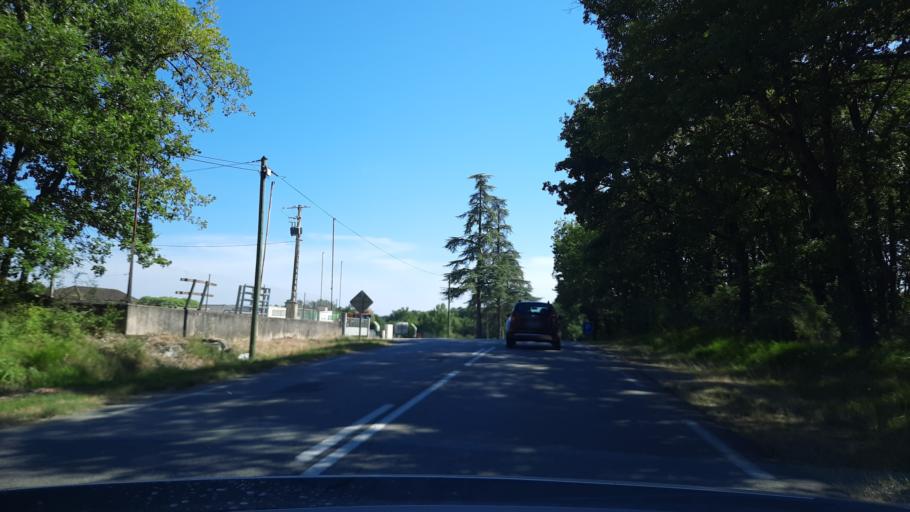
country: FR
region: Midi-Pyrenees
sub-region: Departement du Tarn-et-Garonne
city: Caylus
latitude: 44.3035
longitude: 1.8788
